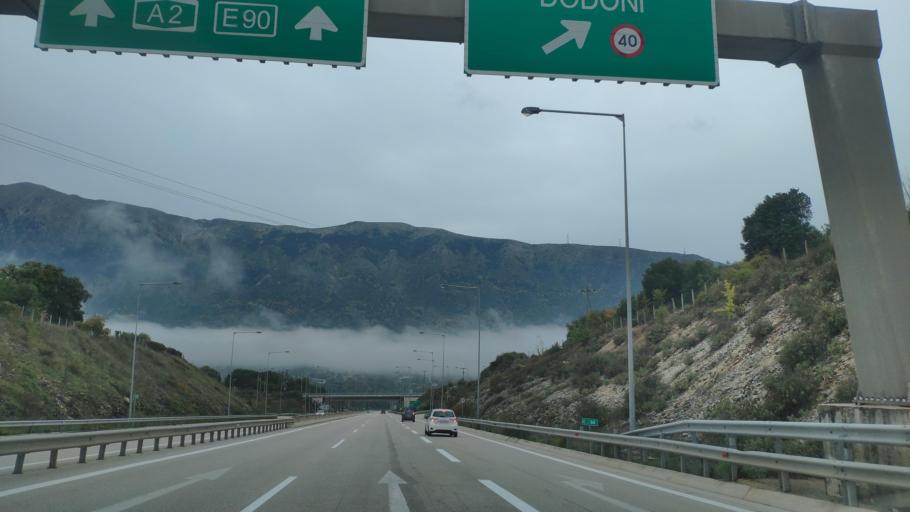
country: GR
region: Epirus
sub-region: Nomos Ioanninon
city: Pedini
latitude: 39.5636
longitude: 20.7777
